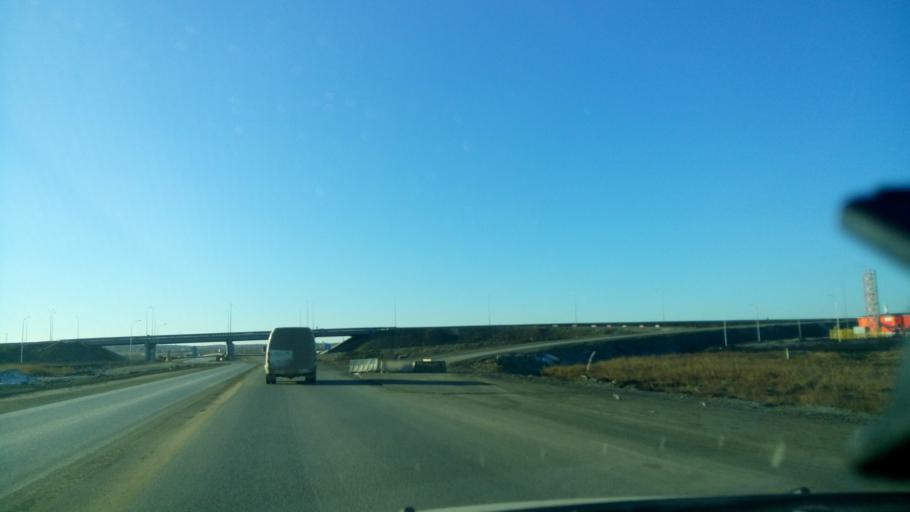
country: RU
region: Sverdlovsk
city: Sovkhoznyy
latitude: 56.7365
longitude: 60.5484
